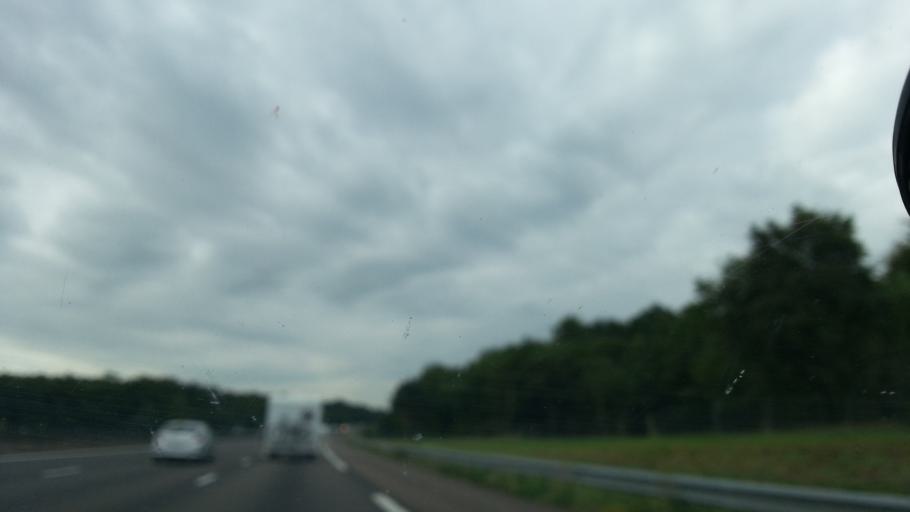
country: FR
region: Bourgogne
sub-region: Departement de Saone-et-Loire
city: Demigny
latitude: 46.8989
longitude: 4.8224
